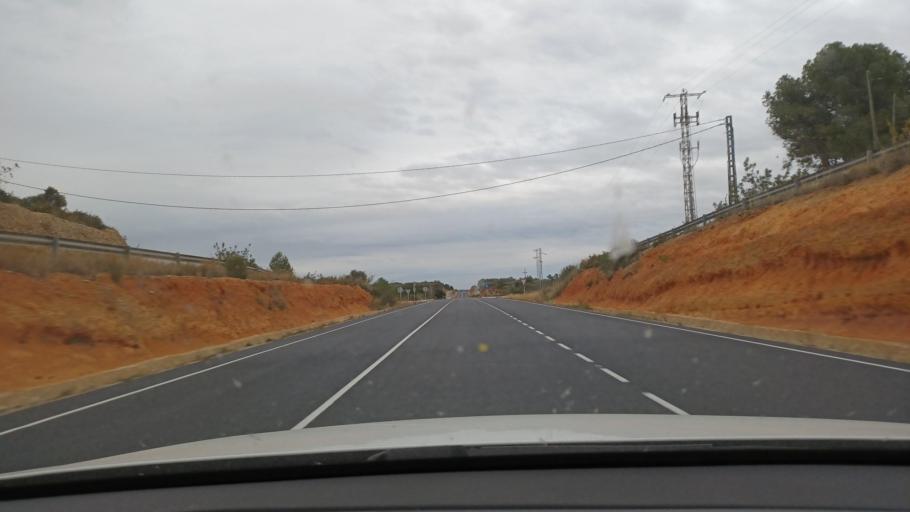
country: ES
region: Valencia
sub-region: Provincia de Castello
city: Traiguera
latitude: 40.5465
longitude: 0.3194
